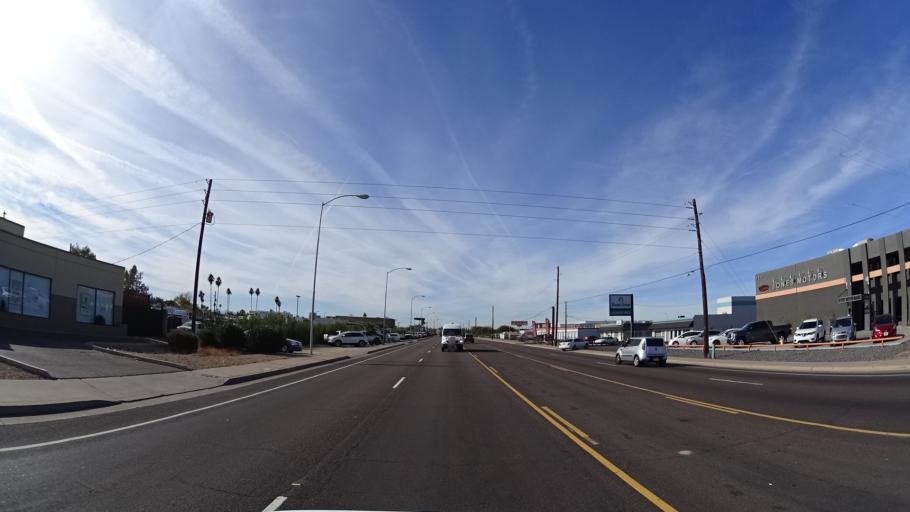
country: US
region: Arizona
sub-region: Maricopa County
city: Mesa
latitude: 33.4075
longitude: -111.8624
